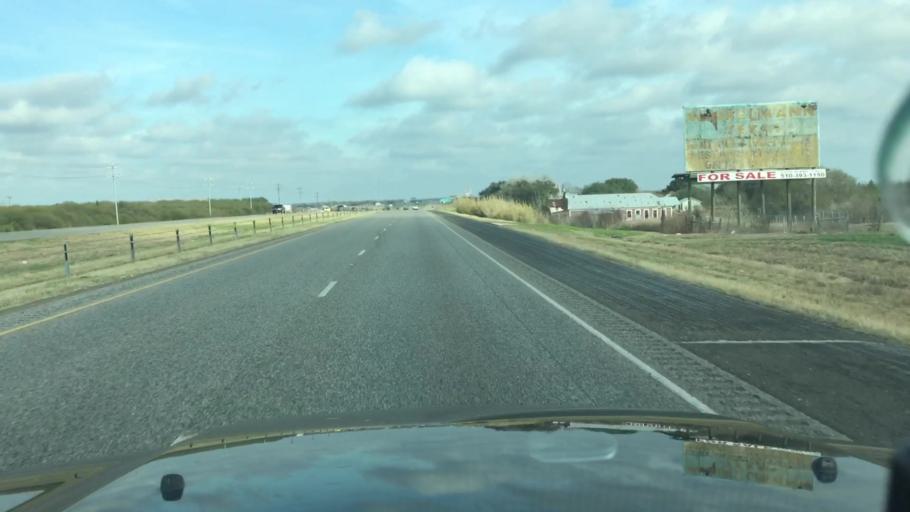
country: US
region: Texas
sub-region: Washington County
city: Brenham
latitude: 30.1381
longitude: -96.3206
